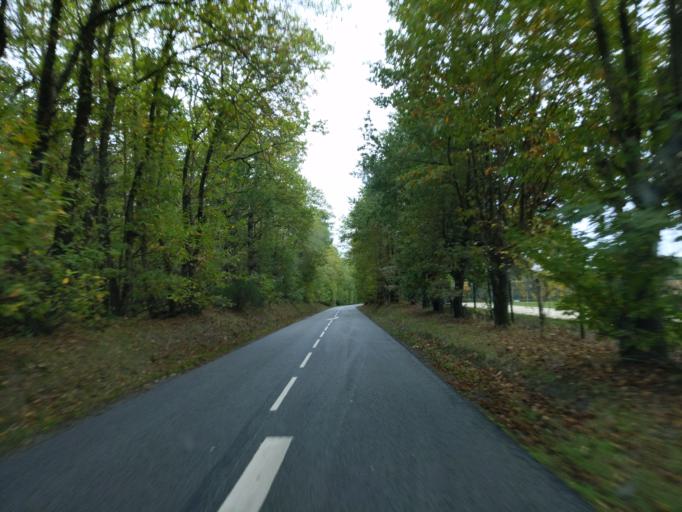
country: FR
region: Ile-de-France
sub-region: Departement des Yvelines
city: Bullion
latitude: 48.6102
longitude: 1.9974
